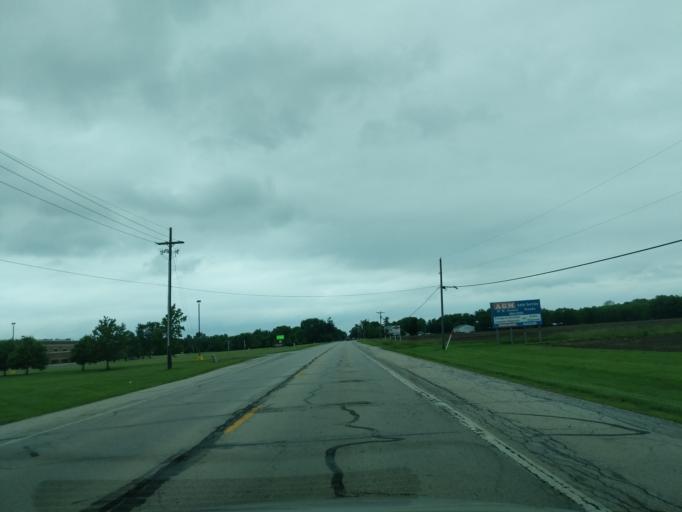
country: US
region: Indiana
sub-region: Hamilton County
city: Arcadia
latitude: 40.1633
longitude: -86.0132
